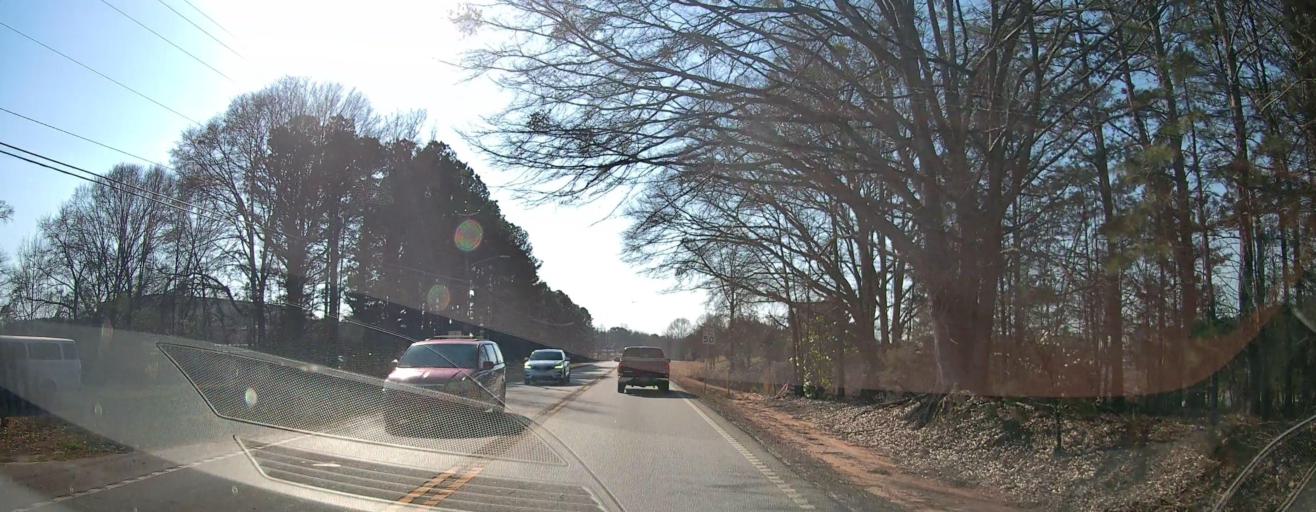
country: US
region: Georgia
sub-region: Henry County
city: Locust Grove
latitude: 33.3207
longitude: -84.0481
